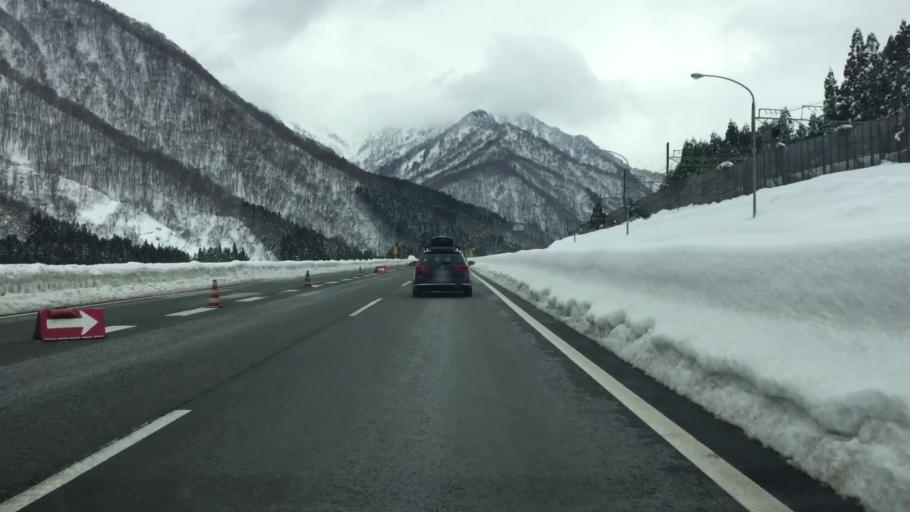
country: JP
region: Niigata
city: Shiozawa
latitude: 36.8781
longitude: 138.8585
